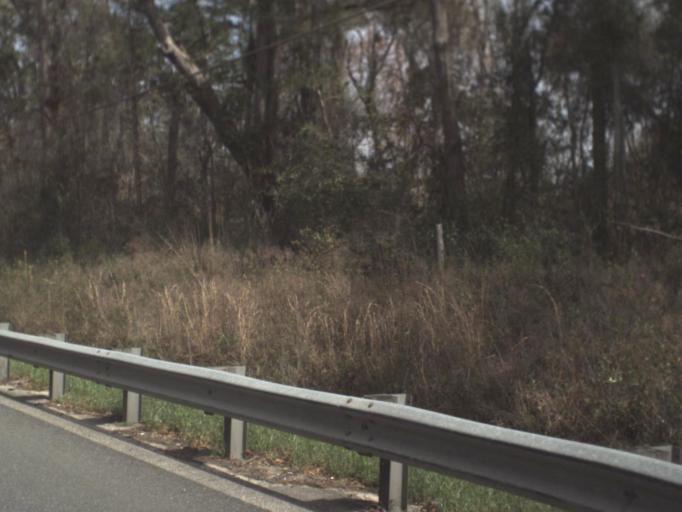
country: US
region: Florida
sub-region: Gadsden County
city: Midway
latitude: 30.5059
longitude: -84.3619
